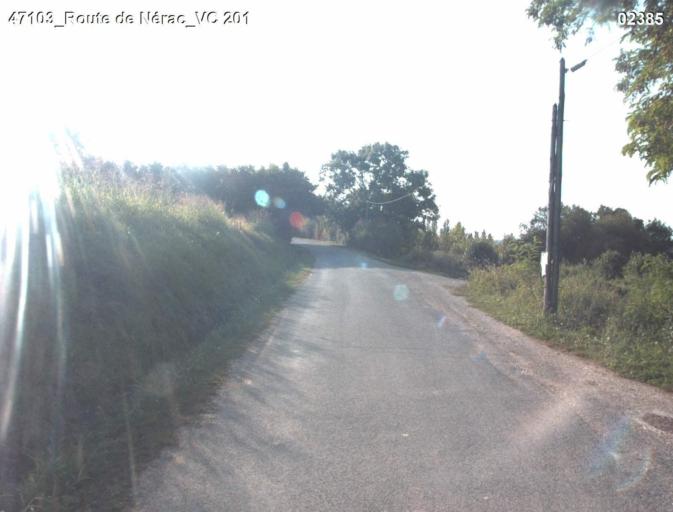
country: FR
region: Aquitaine
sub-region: Departement du Lot-et-Garonne
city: Nerac
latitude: 44.0850
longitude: 0.3234
